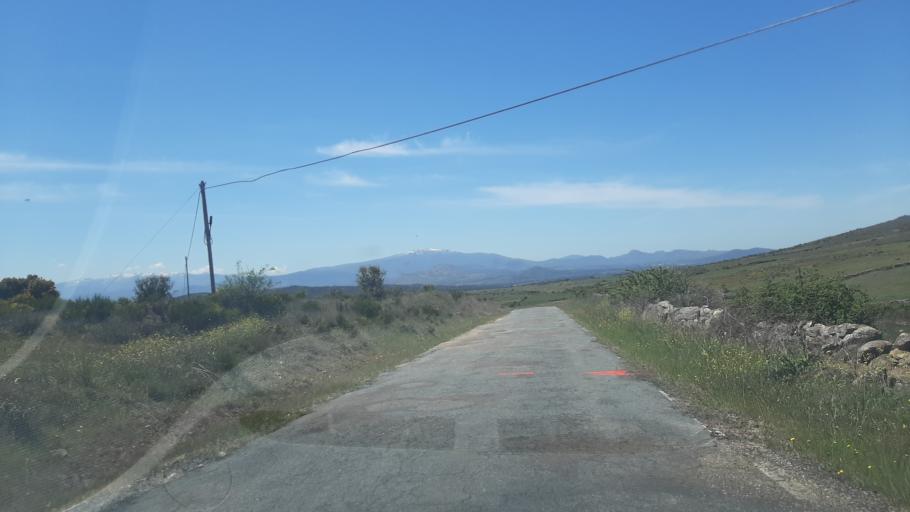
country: ES
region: Castille and Leon
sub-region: Provincia de Avila
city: Narrillos del Alamo
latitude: 40.5622
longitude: -5.4380
